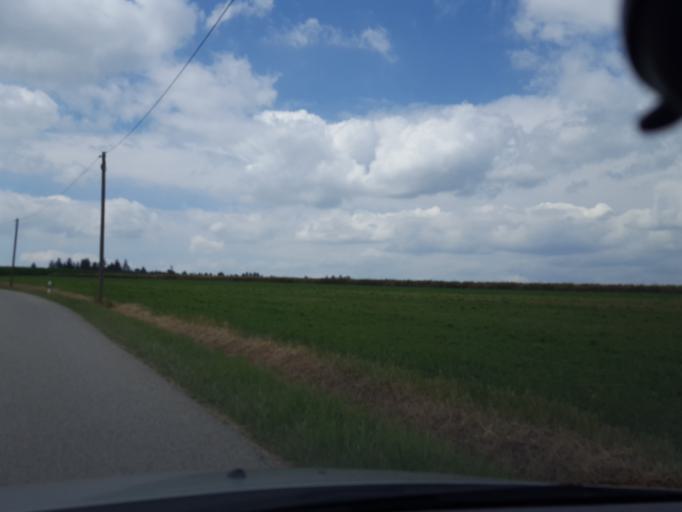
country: DE
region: Bavaria
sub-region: Upper Bavaria
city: Egglkofen
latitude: 48.3941
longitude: 12.4828
